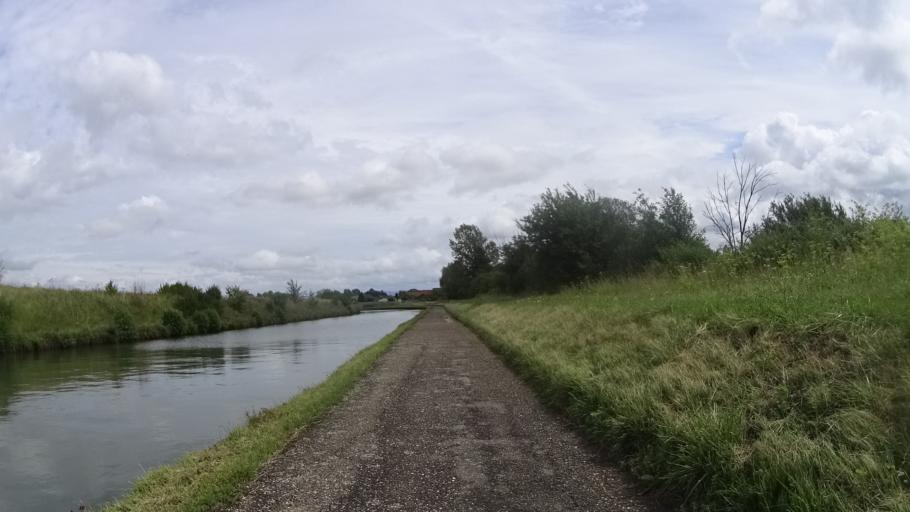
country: FR
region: Lorraine
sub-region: Departement de la Moselle
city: Lorquin
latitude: 48.6897
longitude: 6.9216
